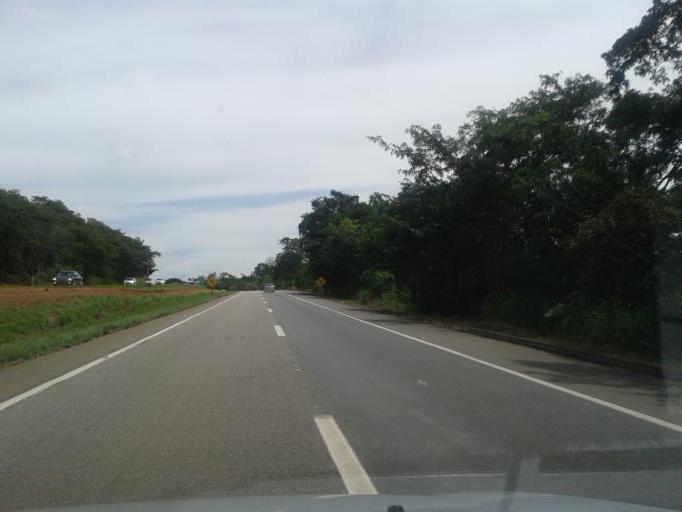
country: BR
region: Goias
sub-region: Hidrolandia
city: Hidrolandia
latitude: -17.0796
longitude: -49.2241
